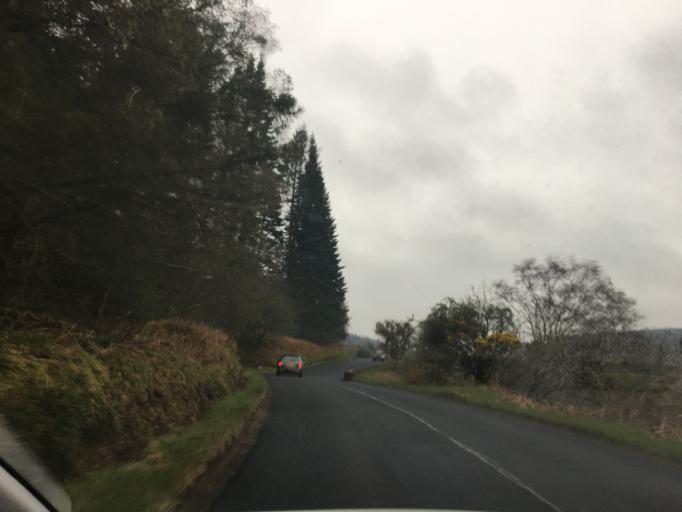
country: GB
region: Scotland
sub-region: North Ayrshire
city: Lamlash
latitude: 55.5453
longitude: -5.1330
